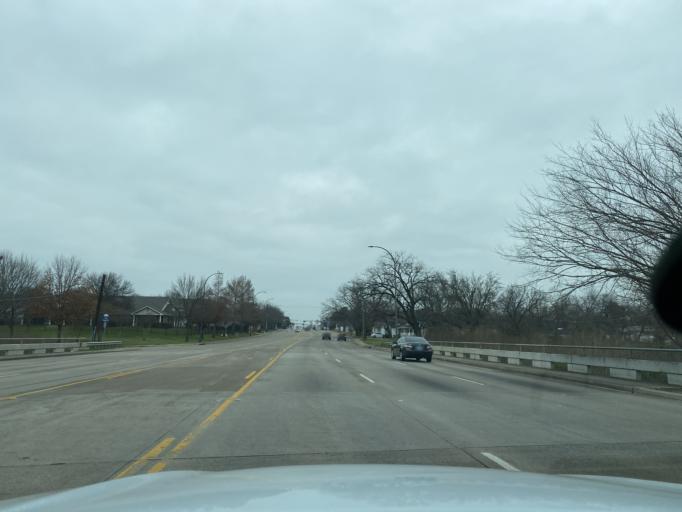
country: US
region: Texas
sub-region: Tarrant County
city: Arlington
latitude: 32.7306
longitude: -97.0974
